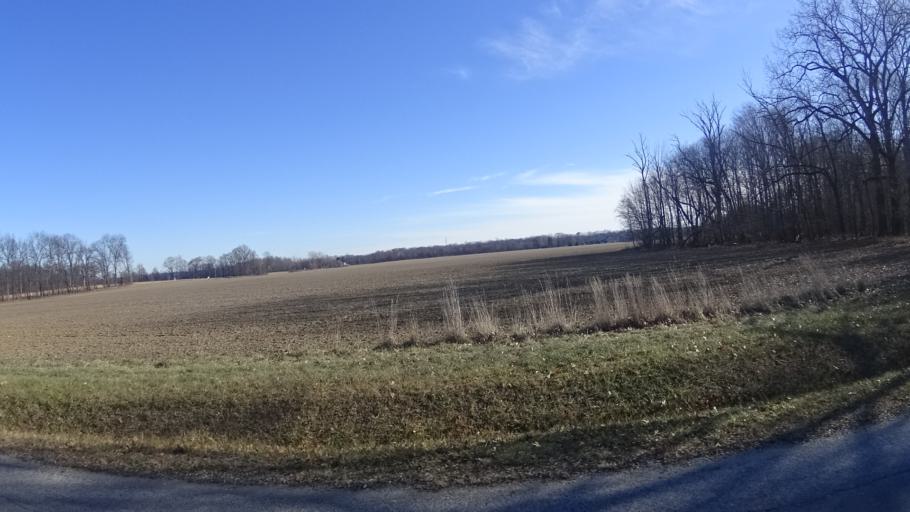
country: US
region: Ohio
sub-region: Lorain County
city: Vermilion-on-the-Lake
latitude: 41.3654
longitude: -82.3286
